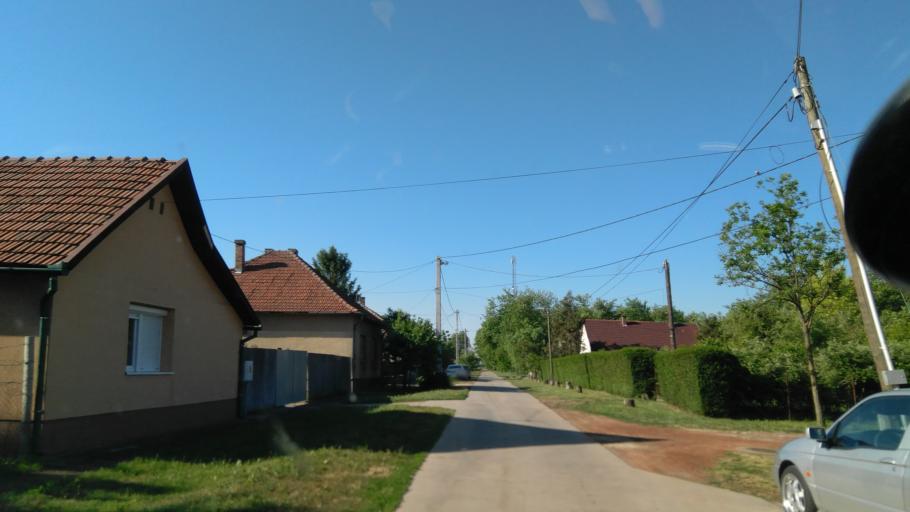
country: HU
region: Bekes
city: Elek
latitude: 46.5328
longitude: 21.2331
